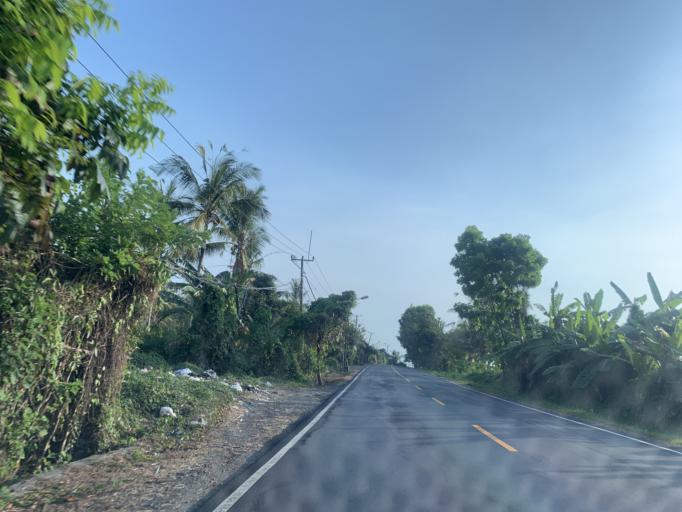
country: ID
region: Bali
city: Banjar Delodrurung
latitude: -8.5118
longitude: 115.0167
